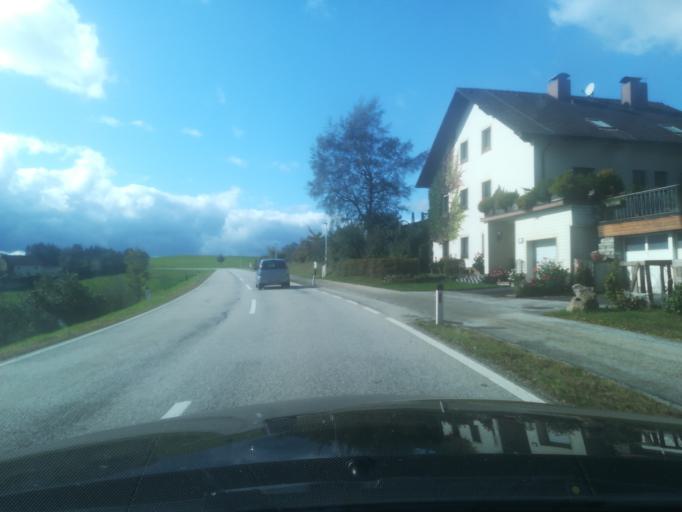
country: AT
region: Upper Austria
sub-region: Politischer Bezirk Urfahr-Umgebung
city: Eidenberg
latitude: 48.3637
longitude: 14.2483
